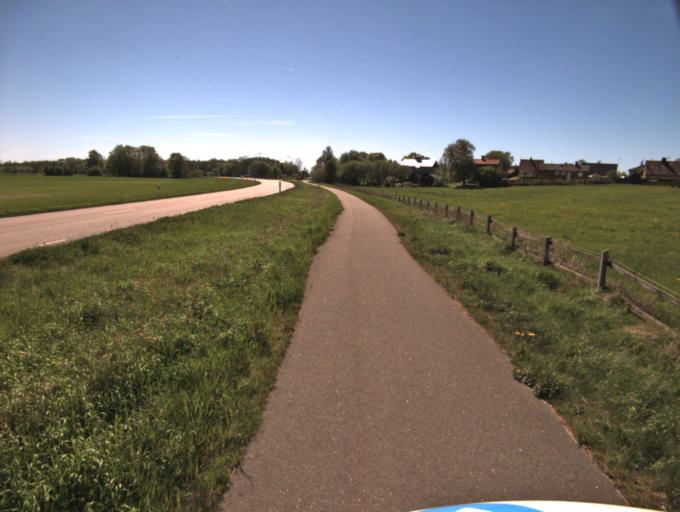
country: SE
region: Skane
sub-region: Kristianstads Kommun
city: Norra Asum
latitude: 55.9927
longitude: 14.1536
